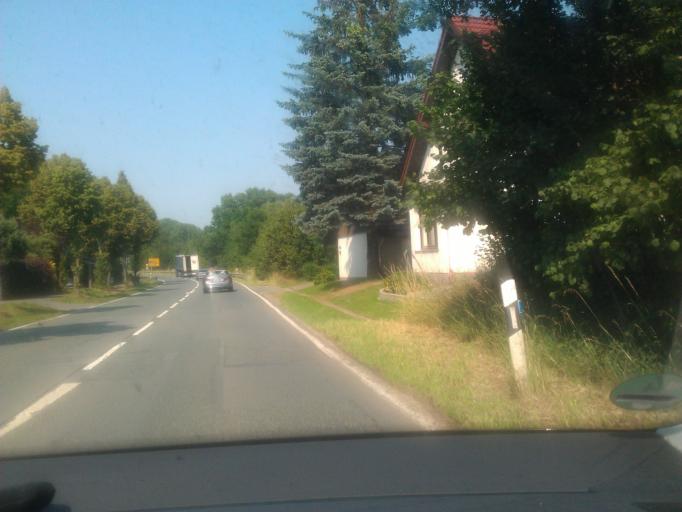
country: DE
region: North Rhine-Westphalia
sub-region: Regierungsbezirk Detmold
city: Bad Salzuflen
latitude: 52.0490
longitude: 8.7381
